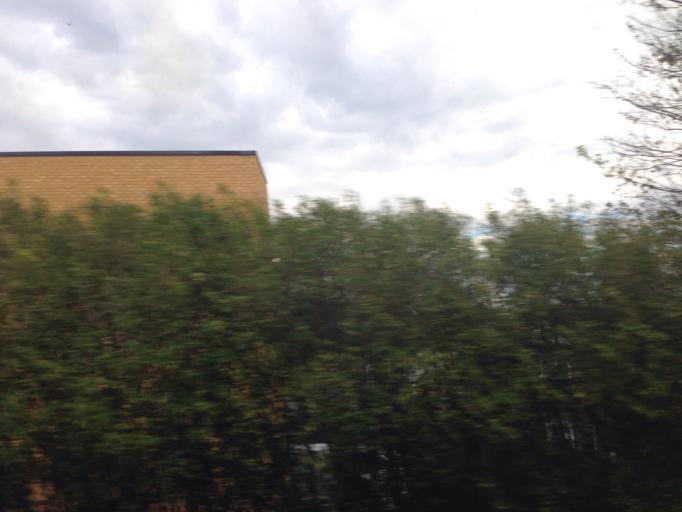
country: GB
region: England
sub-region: Greater London
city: Carshalton
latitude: 51.3751
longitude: -0.1553
